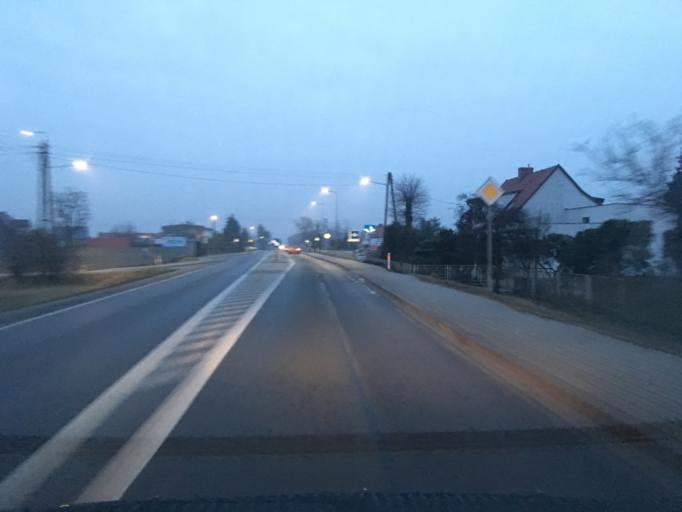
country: PL
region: Lower Silesian Voivodeship
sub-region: Powiat olawski
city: Wierzbno
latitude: 50.9842
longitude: 17.2225
